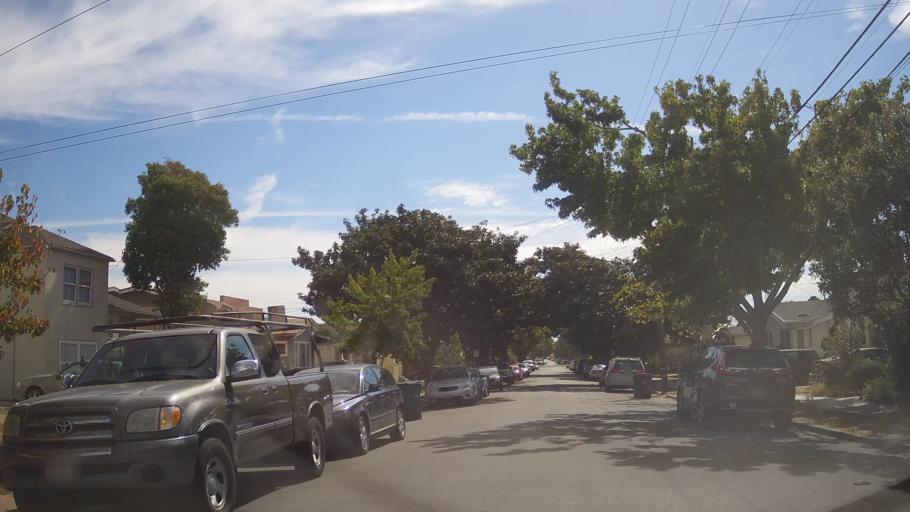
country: US
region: California
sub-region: Alameda County
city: Albany
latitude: 37.8898
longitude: -122.2916
